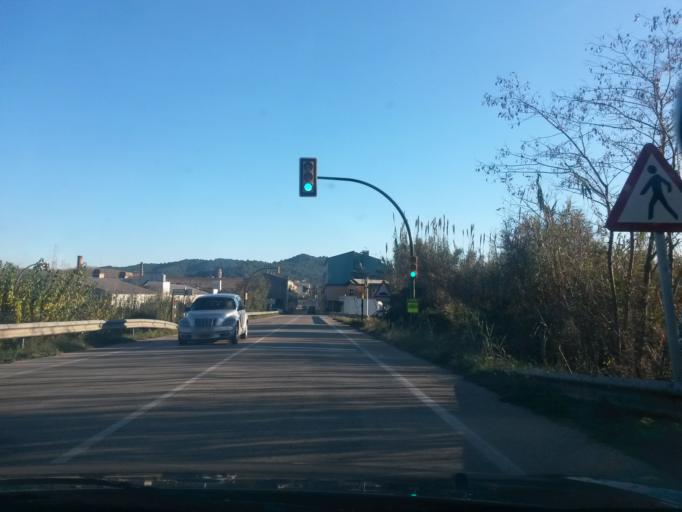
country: ES
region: Catalonia
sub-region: Provincia de Girona
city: Angles
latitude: 41.9615
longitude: 2.6313
